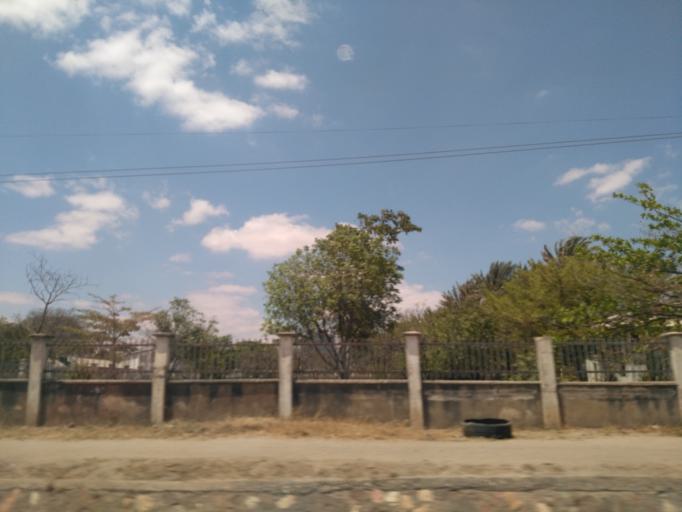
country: TZ
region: Dodoma
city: Dodoma
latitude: -6.1742
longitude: 35.7518
